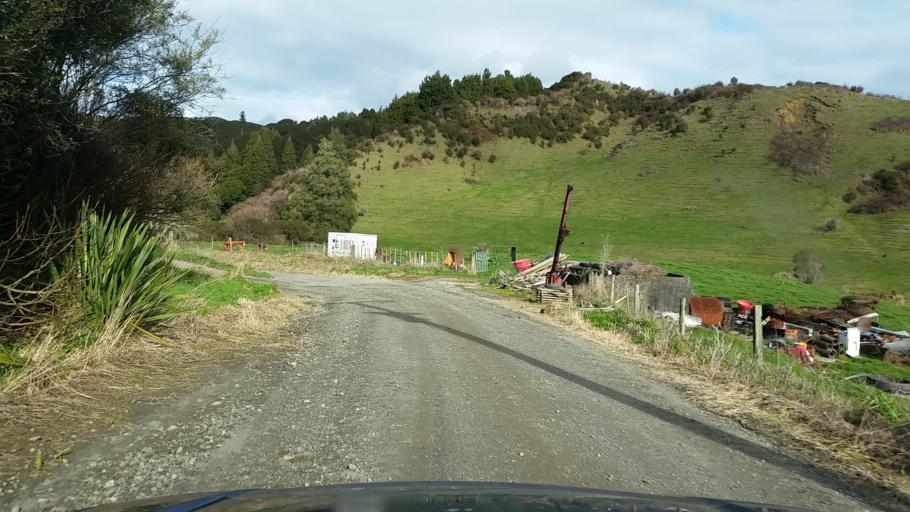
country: NZ
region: Taranaki
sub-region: South Taranaki District
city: Eltham
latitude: -39.2572
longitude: 174.5739
